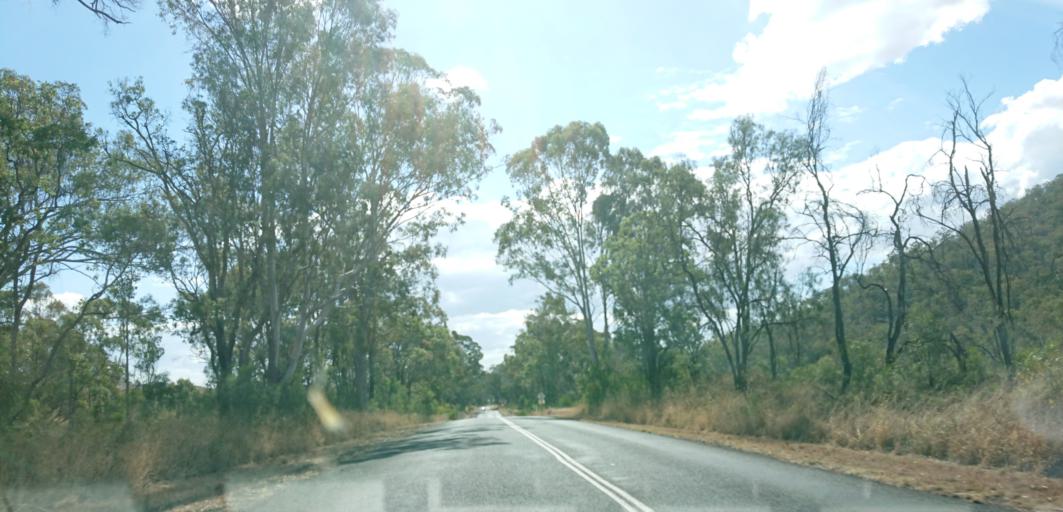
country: AU
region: Queensland
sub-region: Toowoomba
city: Top Camp
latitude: -27.8041
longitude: 152.1073
